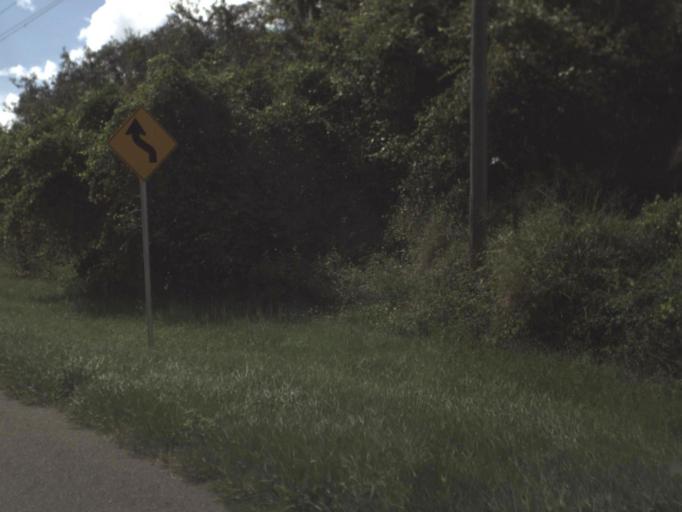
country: US
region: Florida
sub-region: Hardee County
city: Zolfo Springs
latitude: 27.4878
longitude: -81.8451
